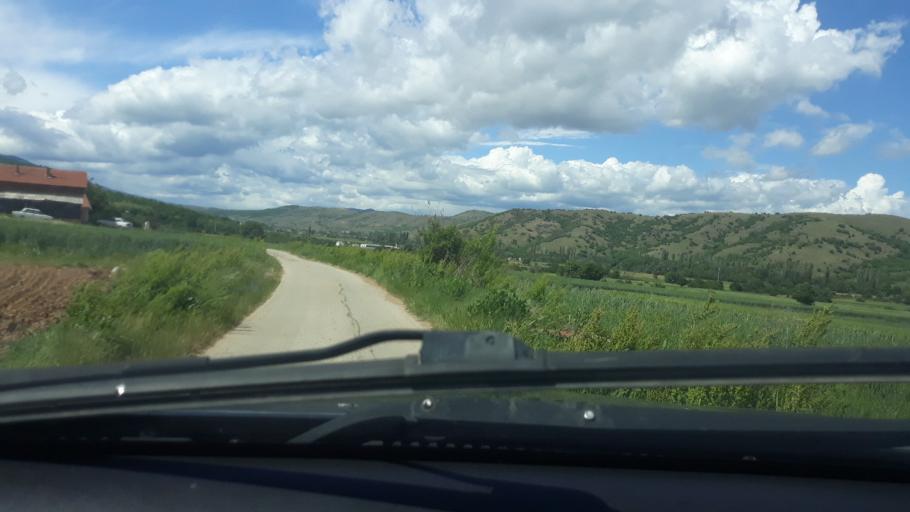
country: MK
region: Krivogastani
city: Krivogashtani
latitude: 41.3391
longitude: 21.3007
